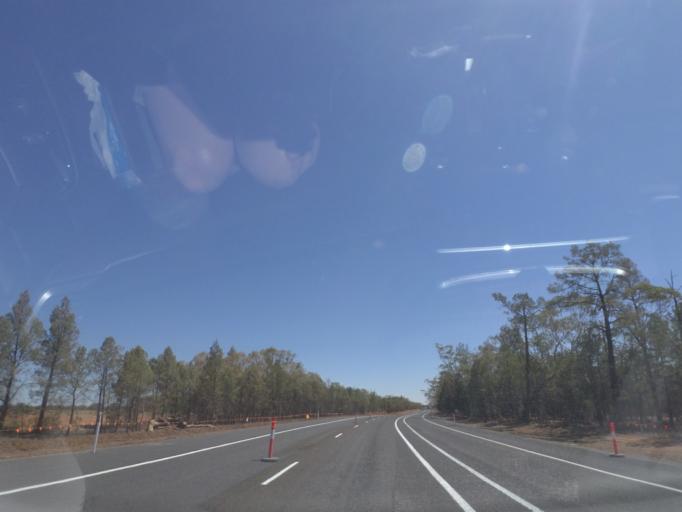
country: AU
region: New South Wales
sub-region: Gilgandra
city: Gilgandra
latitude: -31.6584
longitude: 148.7247
